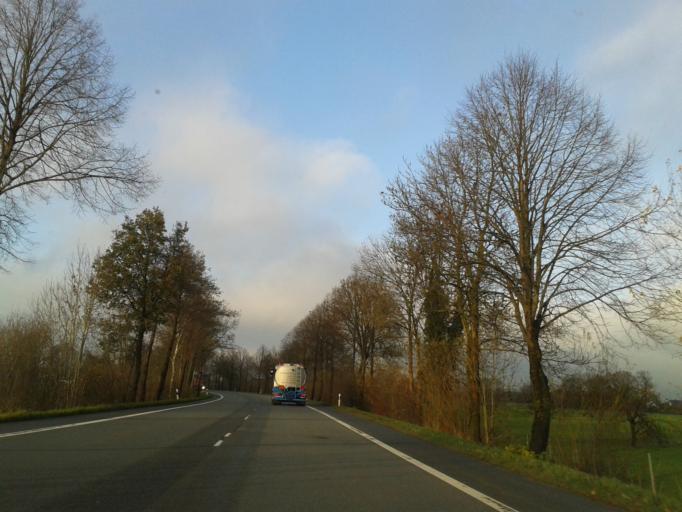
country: DE
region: North Rhine-Westphalia
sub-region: Regierungsbezirk Detmold
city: Oerlinghausen
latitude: 51.8989
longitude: 8.6687
